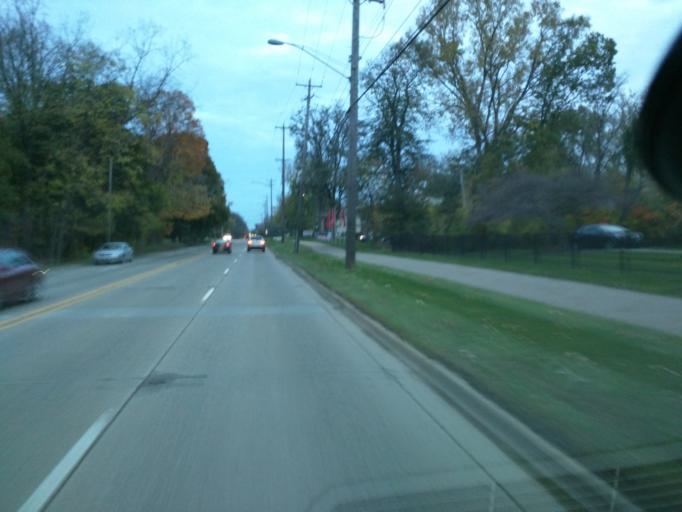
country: US
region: Michigan
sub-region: Eaton County
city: Waverly
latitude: 42.7015
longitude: -84.6030
